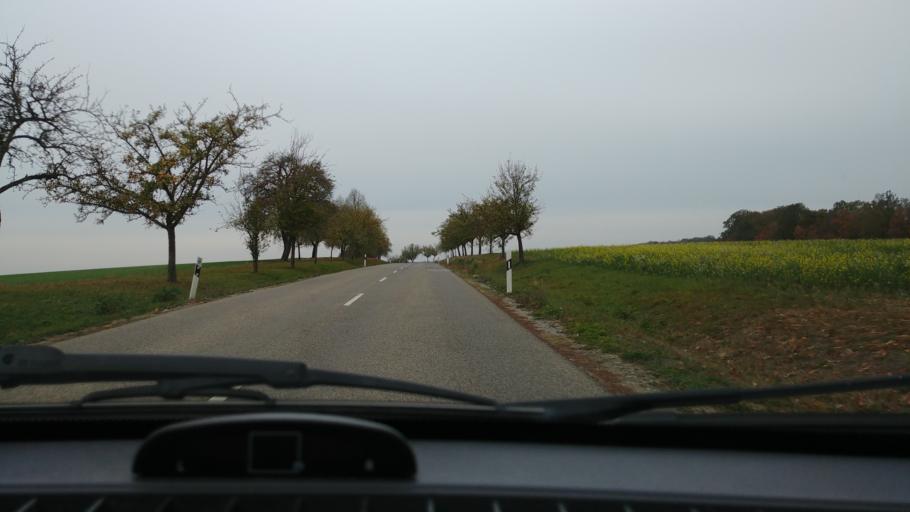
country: DE
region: Baden-Wuerttemberg
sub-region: Regierungsbezirk Stuttgart
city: Schrozberg
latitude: 49.3401
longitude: 10.0508
